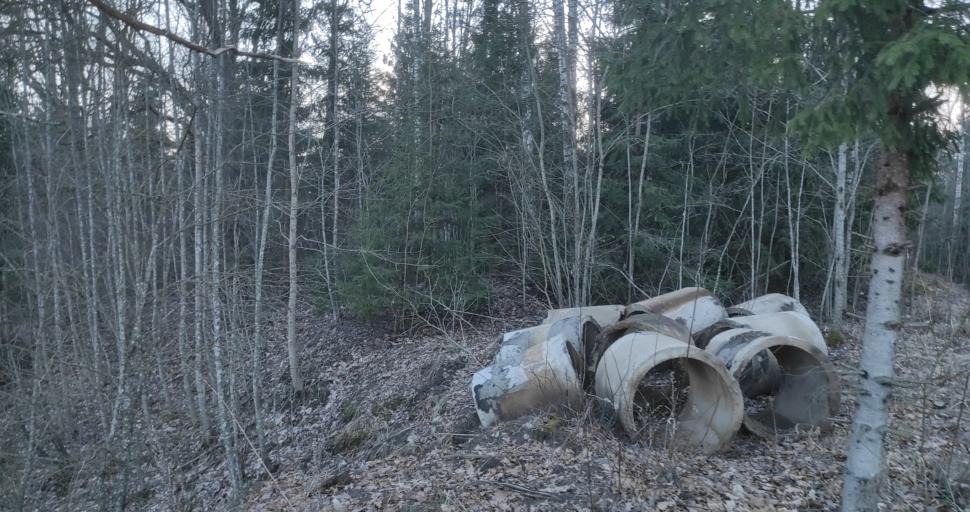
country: LV
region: Kuldigas Rajons
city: Kuldiga
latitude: 56.8098
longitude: 21.8289
